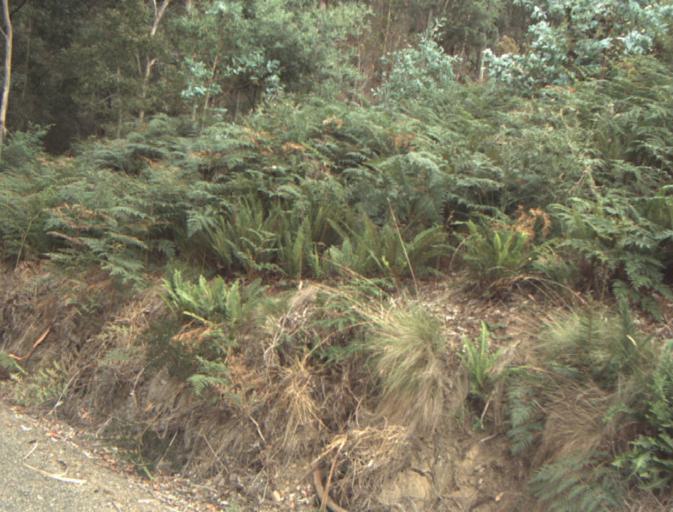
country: AU
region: Tasmania
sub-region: Northern Midlands
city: Evandale
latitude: -41.4559
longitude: 147.4718
